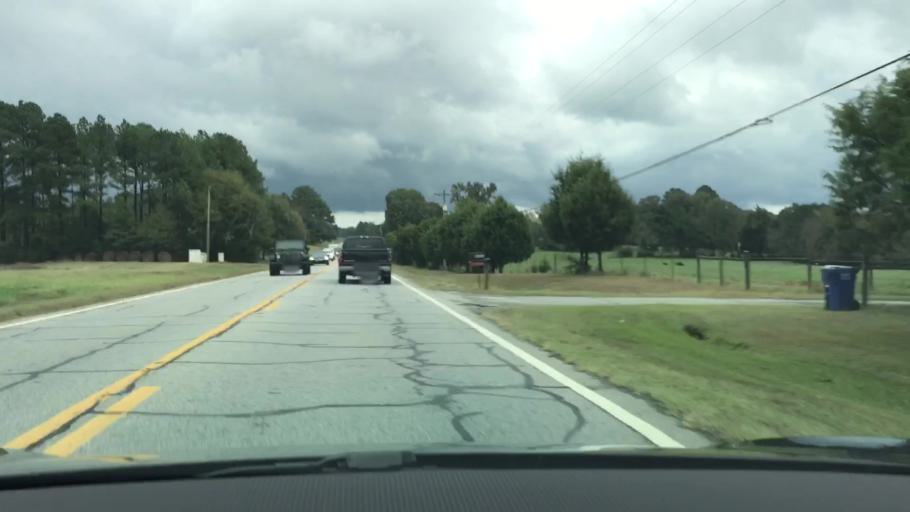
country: US
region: Georgia
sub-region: Oconee County
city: Watkinsville
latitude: 33.7983
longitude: -83.3338
